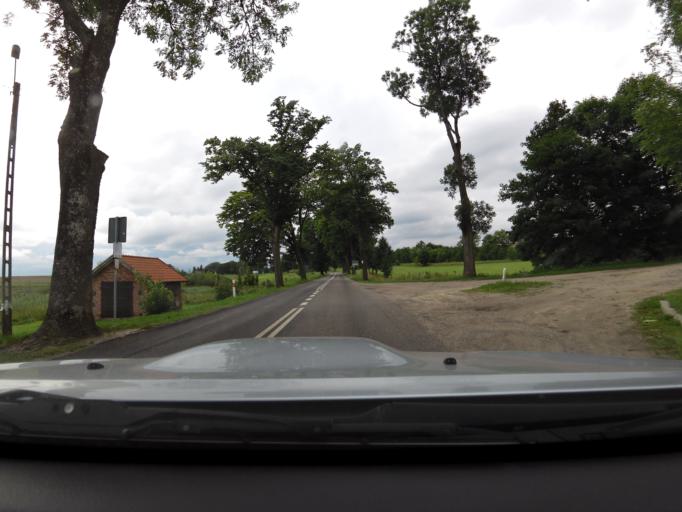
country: PL
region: Warmian-Masurian Voivodeship
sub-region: Powiat ketrzynski
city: Reszel
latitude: 54.0453
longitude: 21.2505
